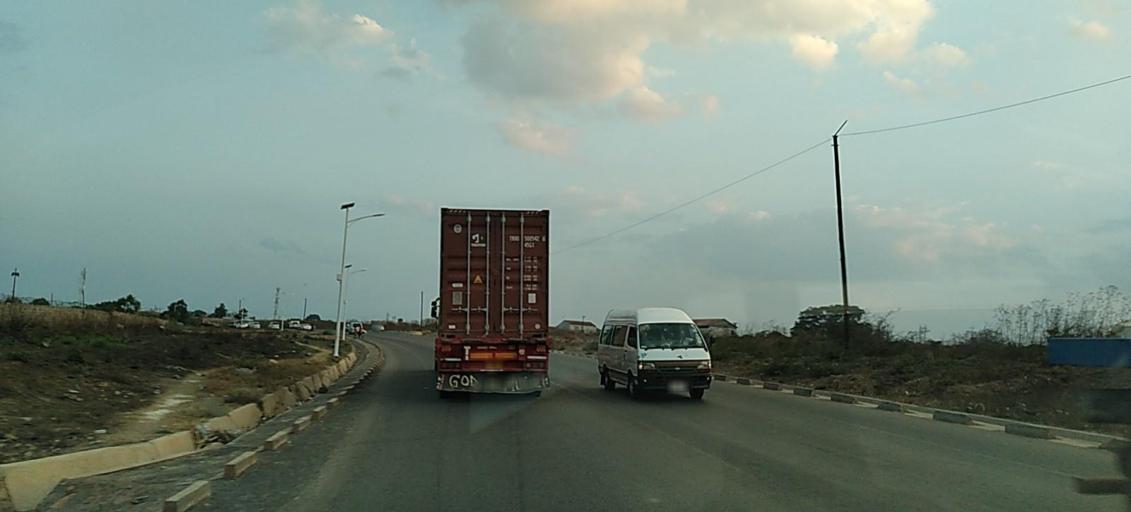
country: ZM
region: Copperbelt
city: Chingola
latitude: -12.5377
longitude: 27.8396
